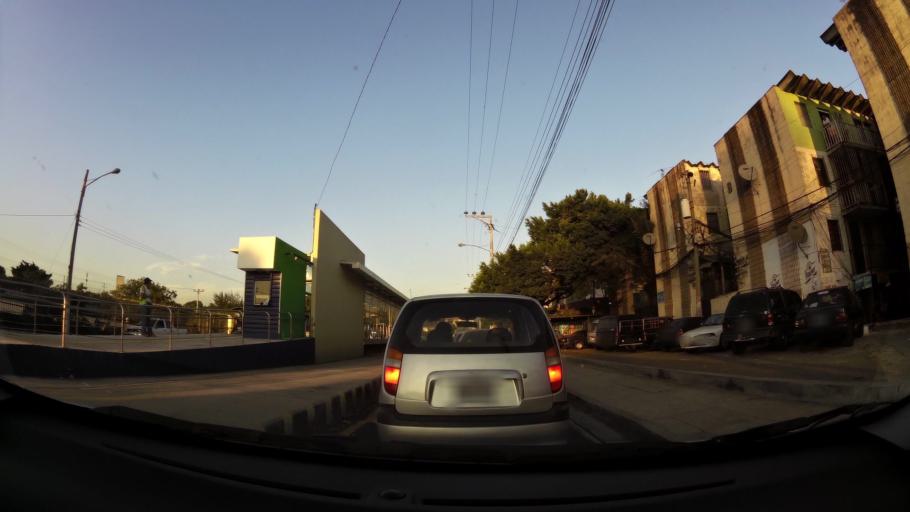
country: SV
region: San Salvador
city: San Salvador
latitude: 13.7028
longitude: -89.2072
